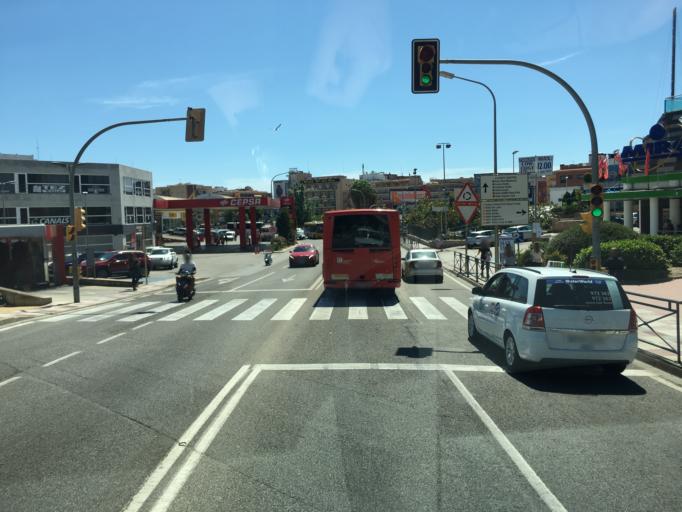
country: ES
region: Catalonia
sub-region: Provincia de Girona
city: Lloret de Mar
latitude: 41.7007
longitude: 2.8391
